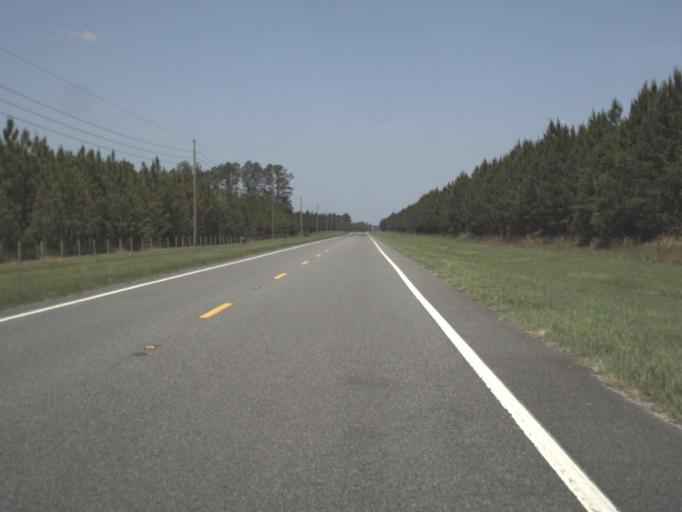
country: US
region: Florida
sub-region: Clay County
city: Asbury Lake
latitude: 29.9779
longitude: -81.8680
